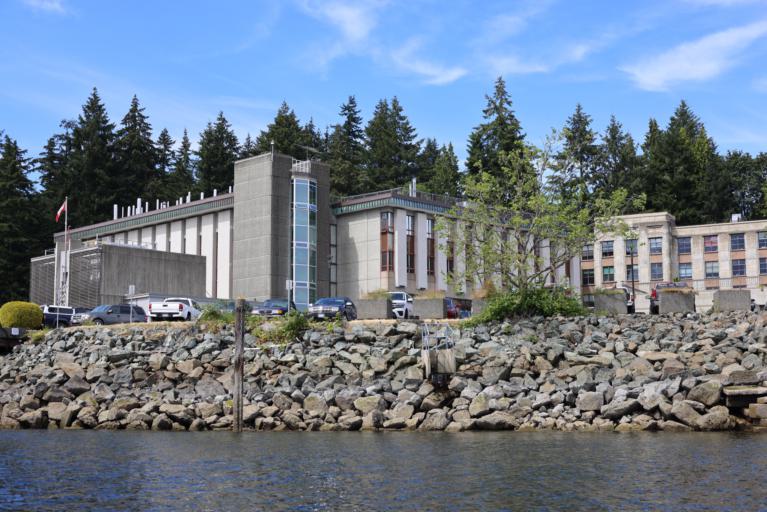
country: CA
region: British Columbia
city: Nanaimo
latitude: 49.2095
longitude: -123.9538
